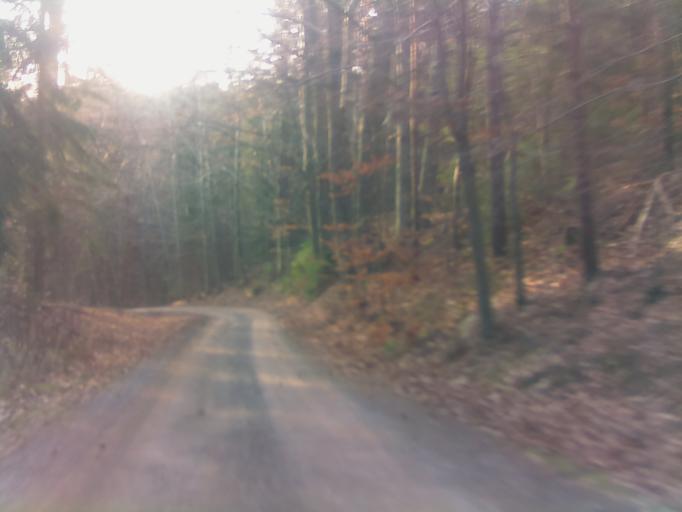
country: DE
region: Thuringia
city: Hummelshain
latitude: 50.7584
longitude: 11.6437
